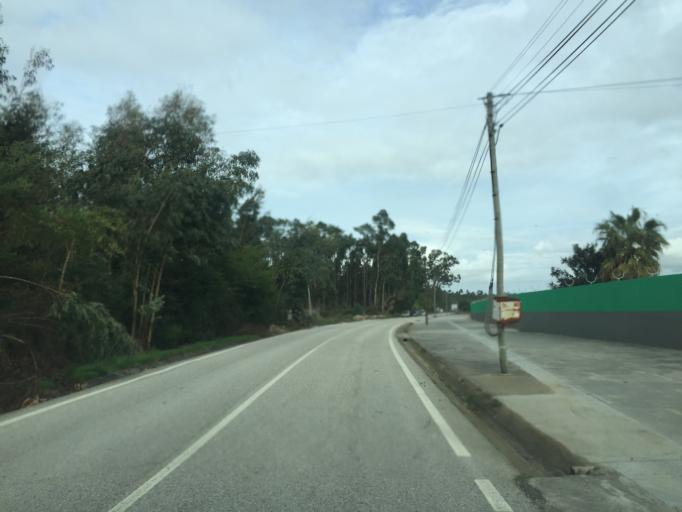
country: PT
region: Coimbra
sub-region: Figueira da Foz
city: Lavos
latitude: 40.0442
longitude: -8.8181
